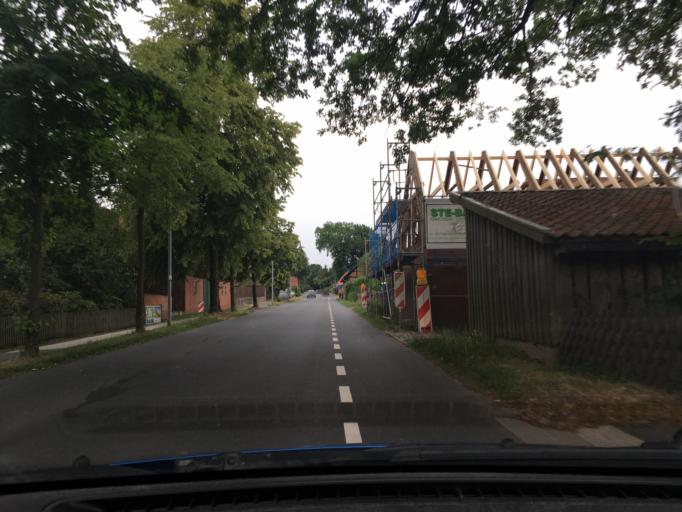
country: DE
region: Lower Saxony
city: Walsrode
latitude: 52.8313
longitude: 9.6295
